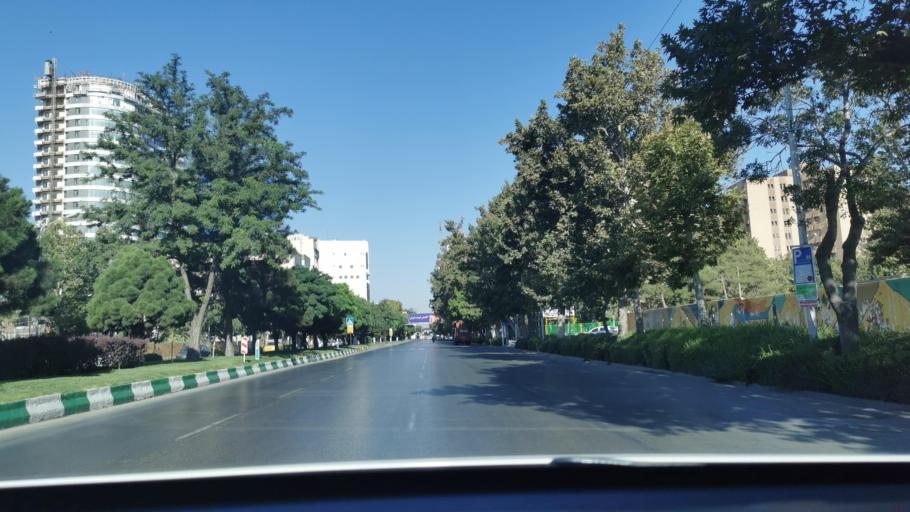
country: IR
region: Razavi Khorasan
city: Mashhad
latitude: 36.3239
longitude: 59.5751
